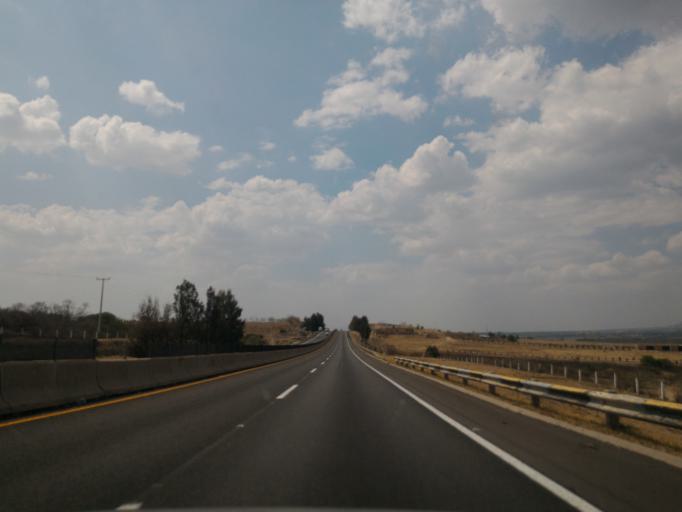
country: MX
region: Jalisco
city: Encarnacion de Diaz
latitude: 21.5155
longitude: -102.2615
